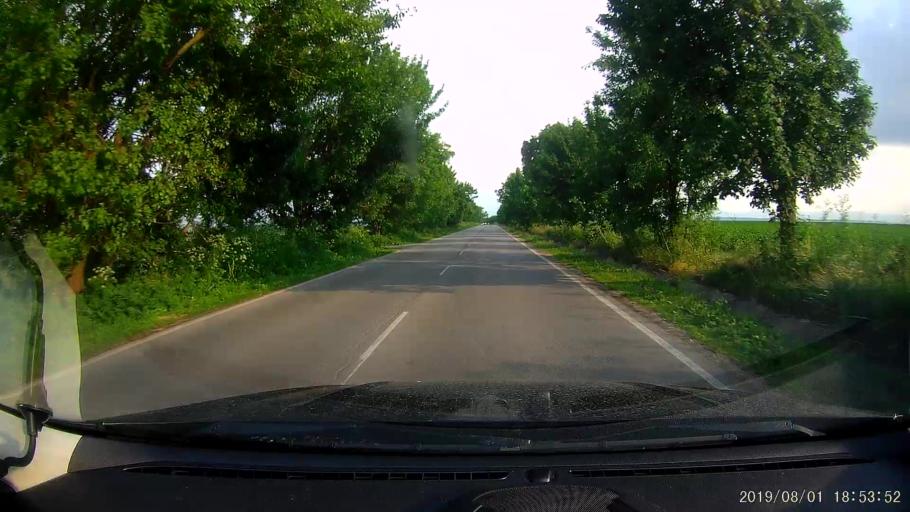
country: BG
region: Shumen
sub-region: Obshtina Shumen
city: Shumen
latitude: 43.2129
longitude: 26.9981
